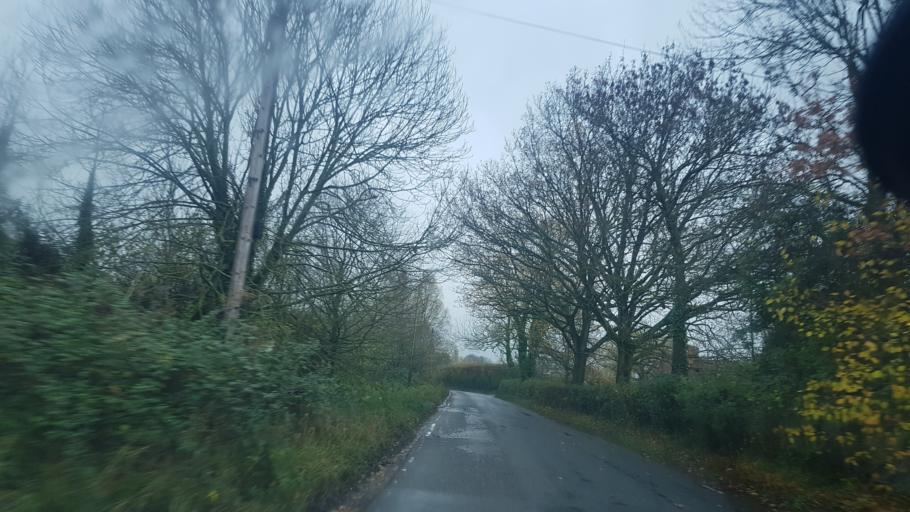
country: GB
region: England
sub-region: Surrey
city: Ripley
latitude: 51.2593
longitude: -0.4830
